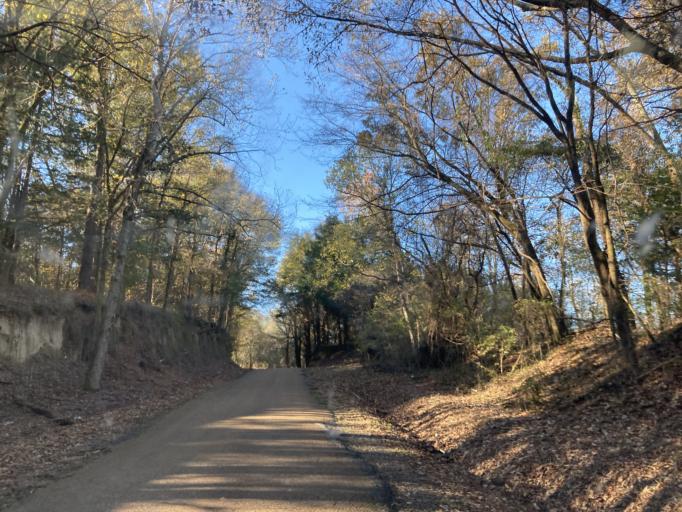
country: US
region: Mississippi
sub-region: Yazoo County
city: Yazoo City
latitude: 32.7215
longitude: -90.5020
